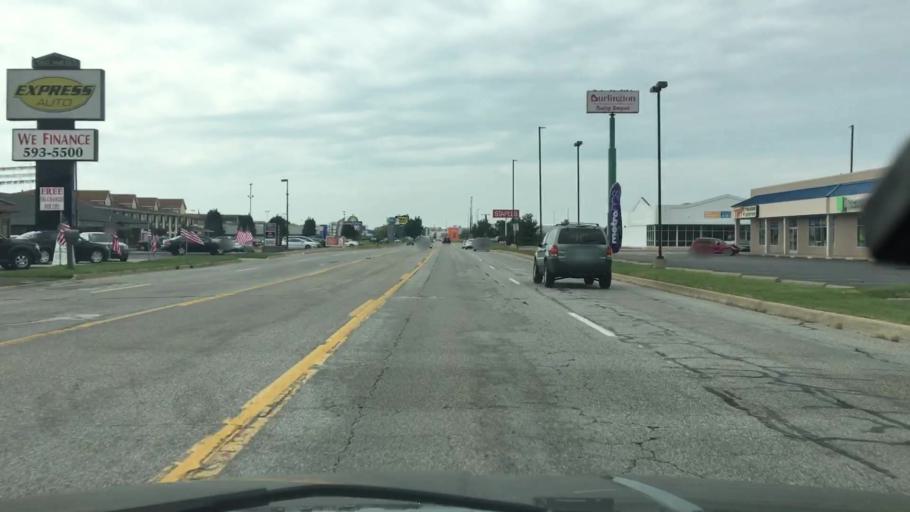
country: US
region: Michigan
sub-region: Berrien County
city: Fair Plain
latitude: 42.0800
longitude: -86.4192
